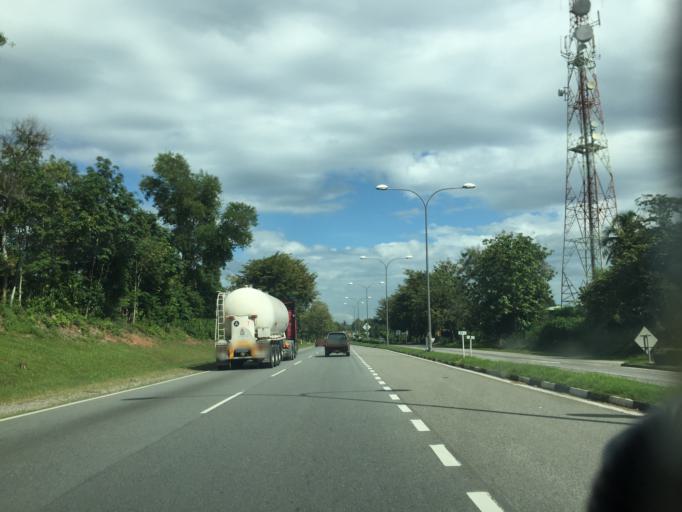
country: MY
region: Kedah
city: Jitra
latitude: 6.3299
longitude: 100.4204
